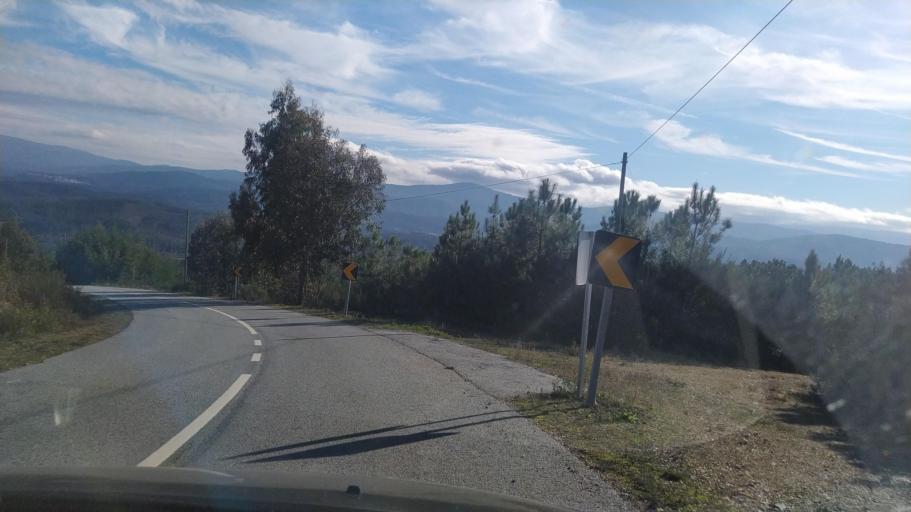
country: PT
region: Castelo Branco
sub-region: Concelho do Fundao
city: Aldeia de Joanes
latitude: 40.1752
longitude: -7.6818
